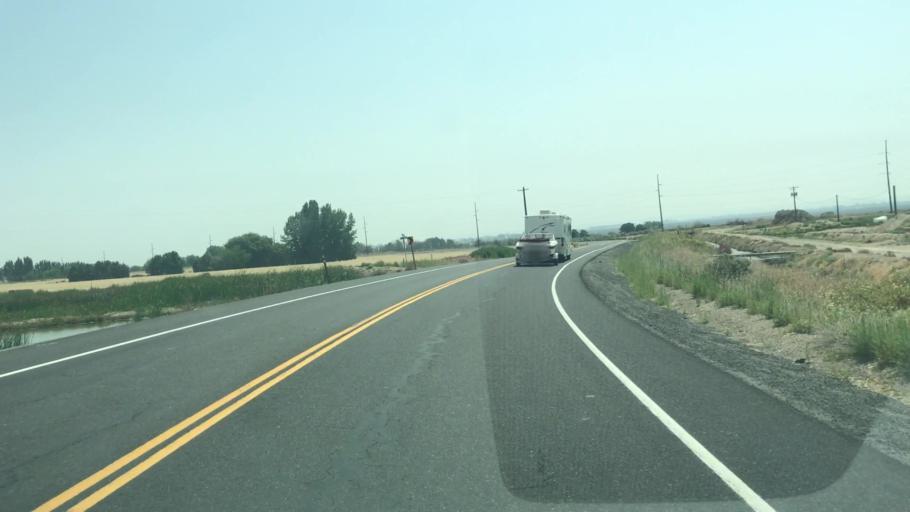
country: US
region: Washington
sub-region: Grant County
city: Quincy
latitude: 47.1631
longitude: -119.9193
